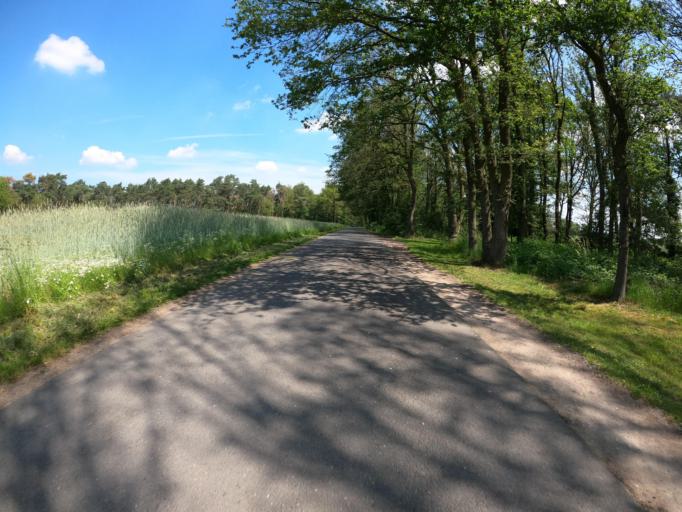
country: DE
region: North Rhine-Westphalia
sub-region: Regierungsbezirk Dusseldorf
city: Hunxe
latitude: 51.7117
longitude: 6.7134
